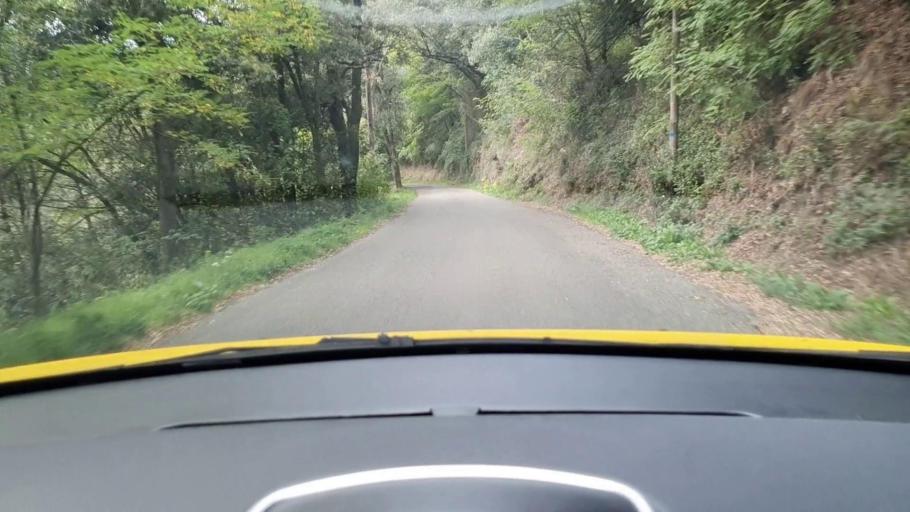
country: FR
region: Languedoc-Roussillon
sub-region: Departement du Gard
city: Sumene
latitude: 44.0097
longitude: 3.6604
